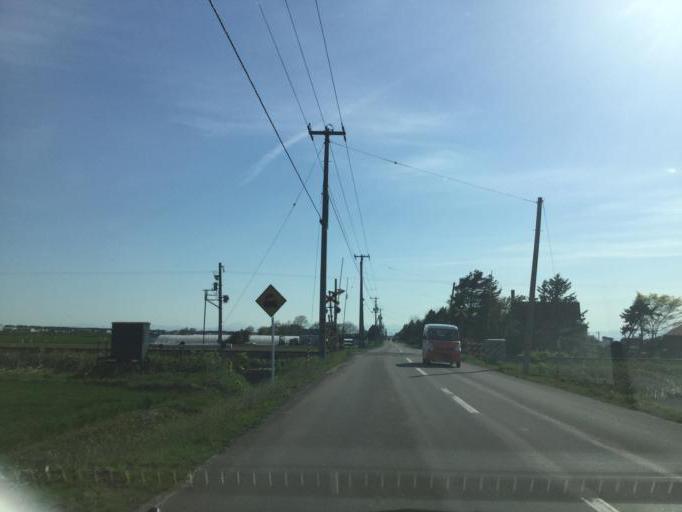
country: JP
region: Hokkaido
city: Iwamizawa
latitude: 43.1695
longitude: 141.7400
